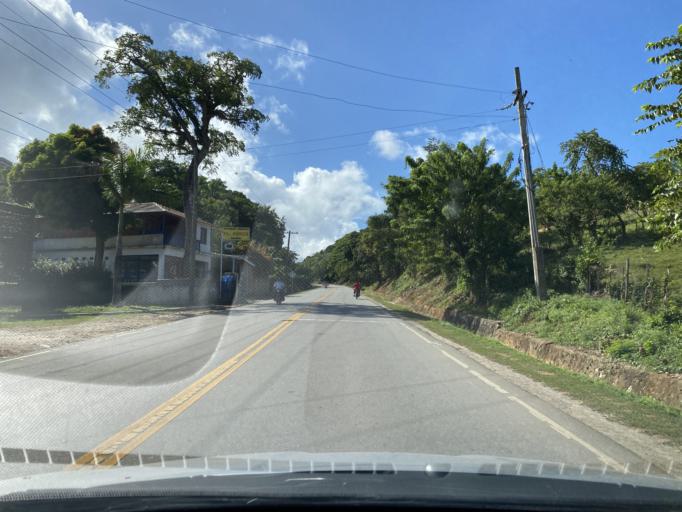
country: DO
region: Samana
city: Las Terrenas
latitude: 19.3109
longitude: -69.5306
